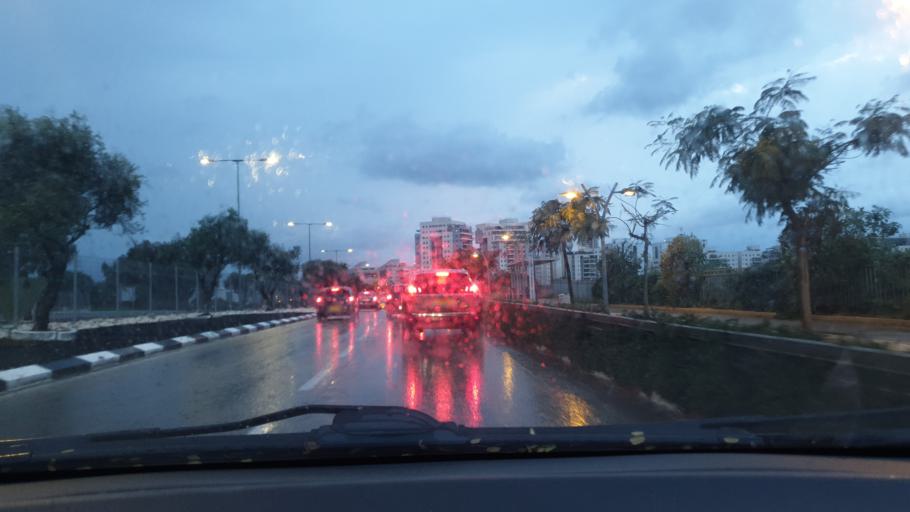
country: IL
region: Central District
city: Bet Dagan
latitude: 31.9689
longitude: 34.8291
